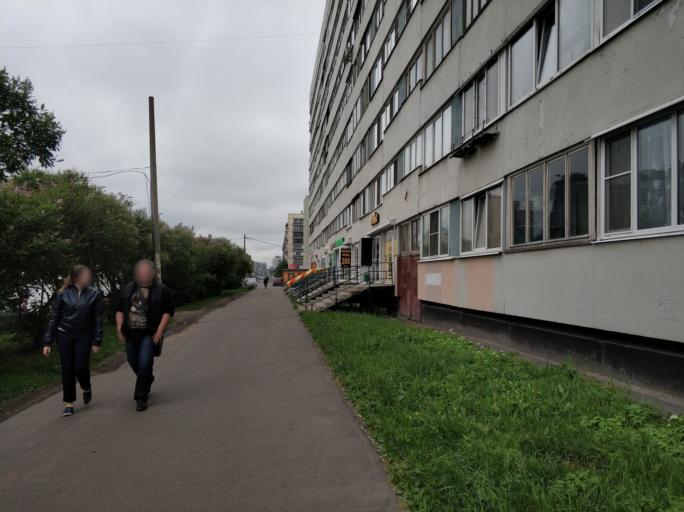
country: RU
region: St.-Petersburg
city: Grazhdanka
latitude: 60.0358
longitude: 30.4105
